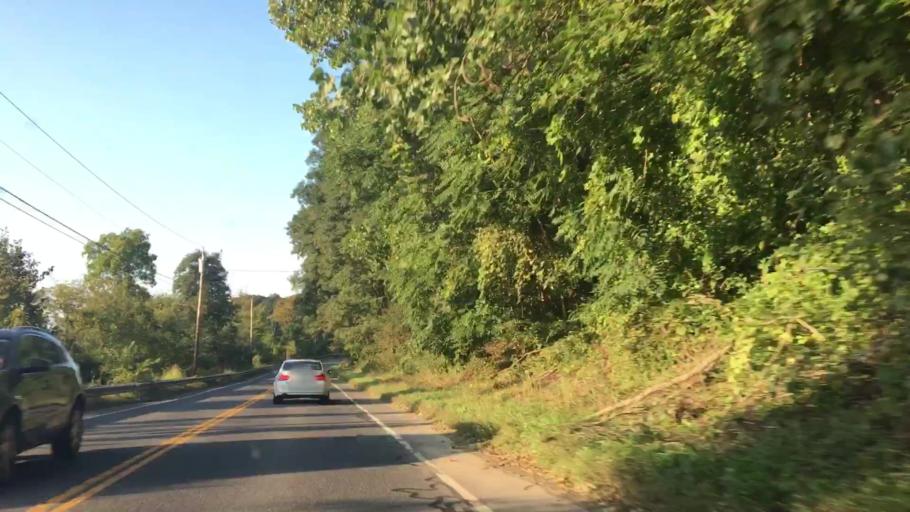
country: US
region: Connecticut
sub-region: Litchfield County
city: New Milford
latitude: 41.5585
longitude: -73.4054
